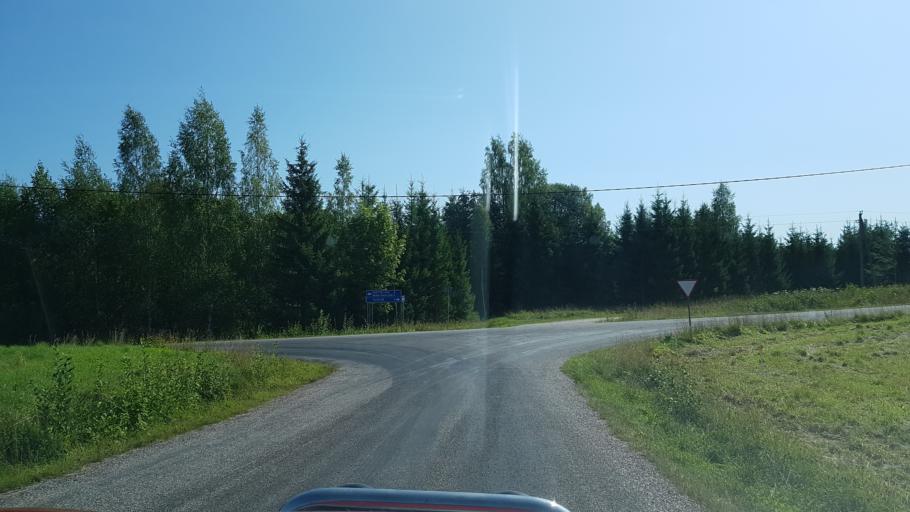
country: EE
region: Vorumaa
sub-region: Voru linn
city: Voru
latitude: 57.7061
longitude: 27.1896
